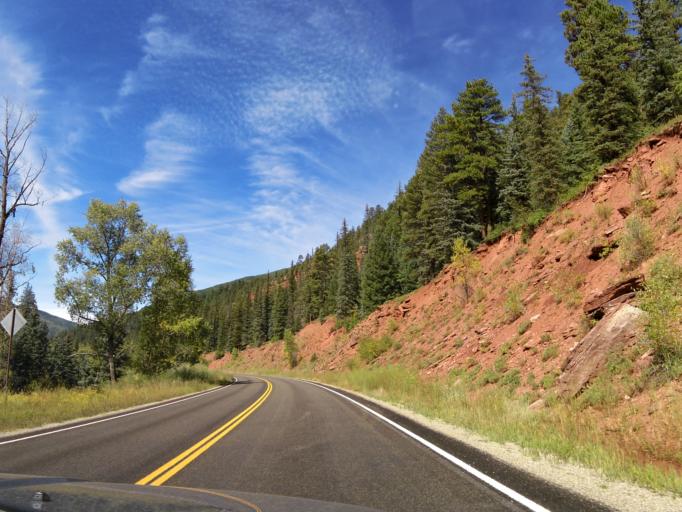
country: US
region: Colorado
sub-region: Montezuma County
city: Mancos
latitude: 37.5881
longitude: -108.1537
